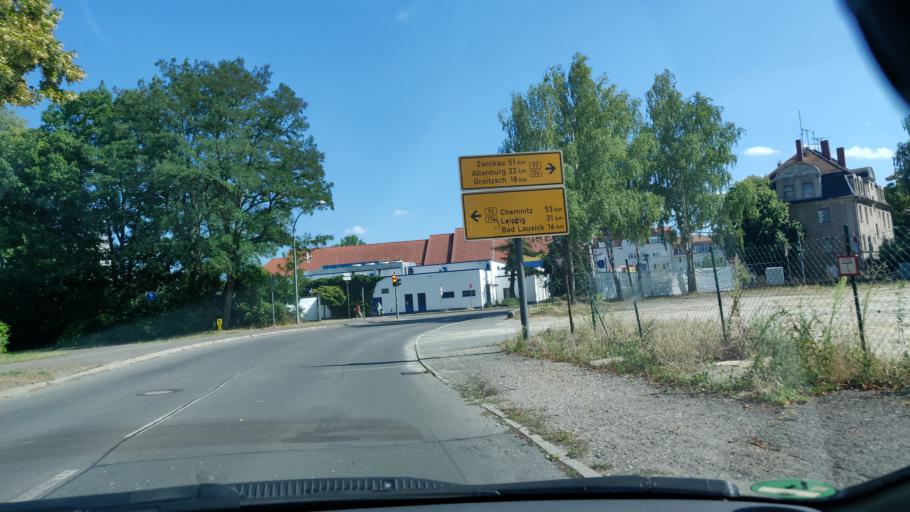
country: DE
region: Saxony
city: Borna
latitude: 51.1260
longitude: 12.4942
